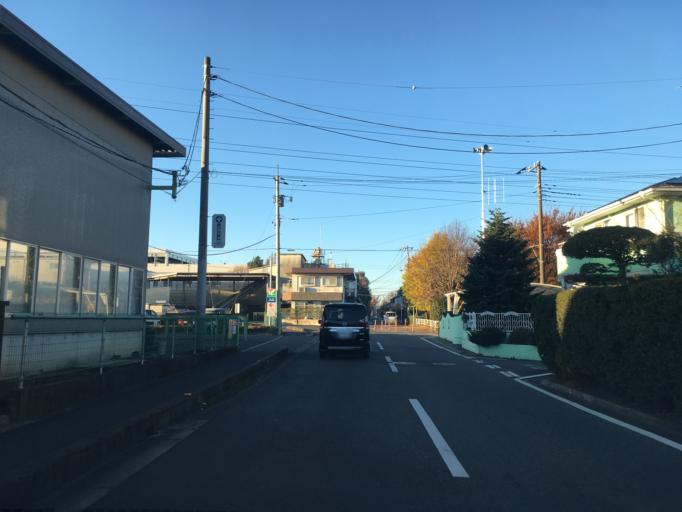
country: JP
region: Saitama
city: Sayama
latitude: 35.8238
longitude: 139.3959
